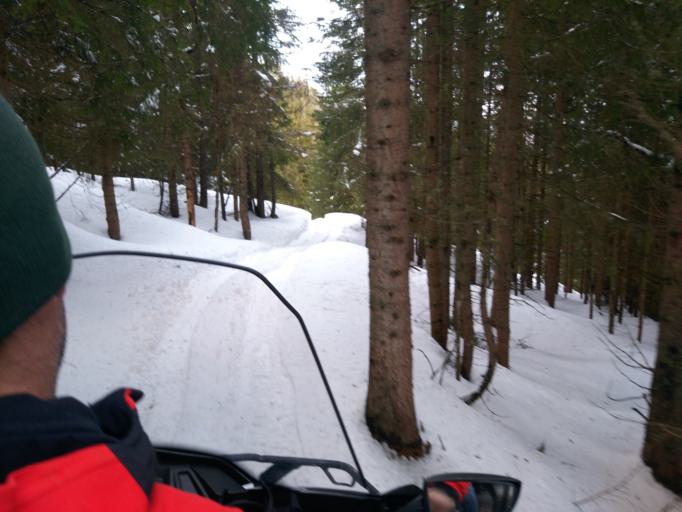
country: IT
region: Veneto
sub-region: Provincia di Belluno
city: Rocca Pietore
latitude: 46.4177
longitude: 11.9857
